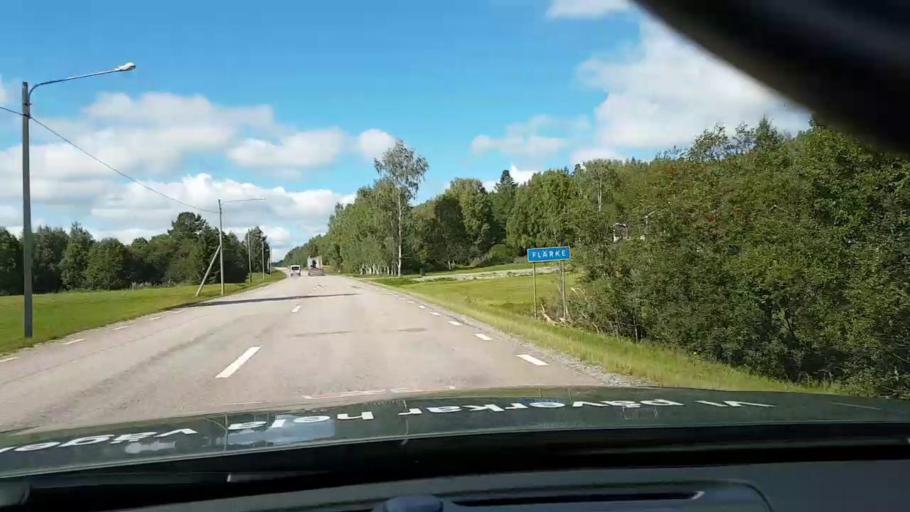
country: SE
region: Vaesternorrland
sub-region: OErnskoeldsviks Kommun
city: Bjasta
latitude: 63.3806
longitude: 18.4138
